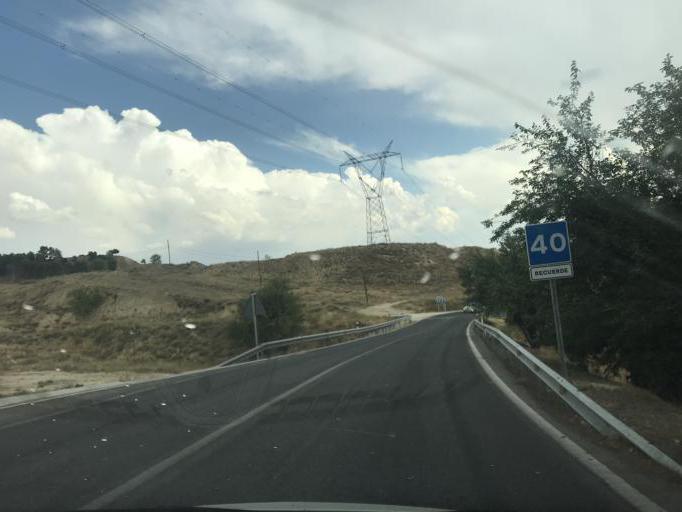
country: ES
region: Madrid
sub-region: Provincia de Madrid
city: Paracuellos de Jarama
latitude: 40.5059
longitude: -3.5379
